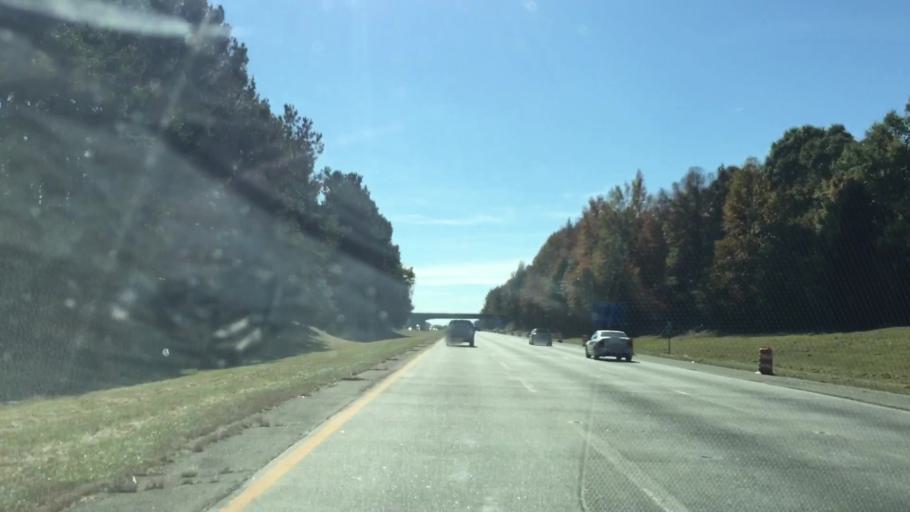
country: US
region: North Carolina
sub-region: Davidson County
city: Lexington
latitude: 35.8208
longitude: -80.1722
